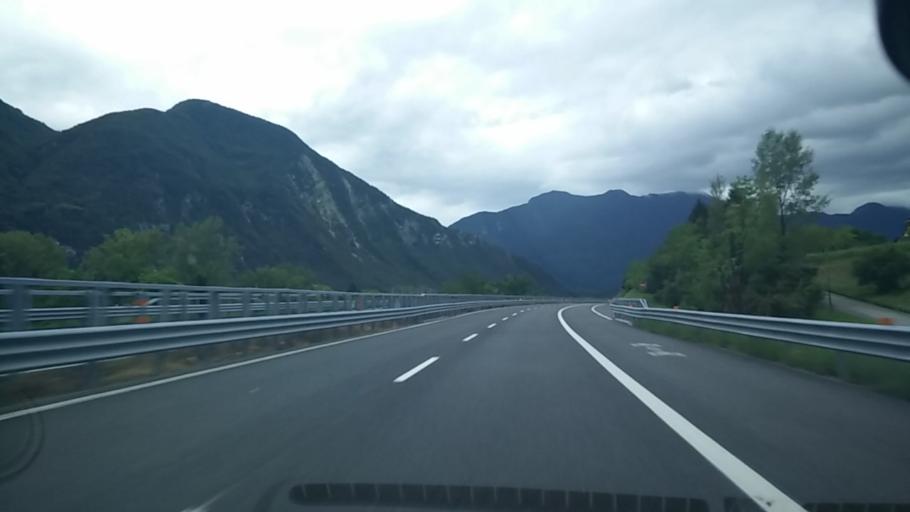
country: IT
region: Friuli Venezia Giulia
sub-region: Provincia di Udine
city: Amaro
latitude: 46.3734
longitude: 13.1039
